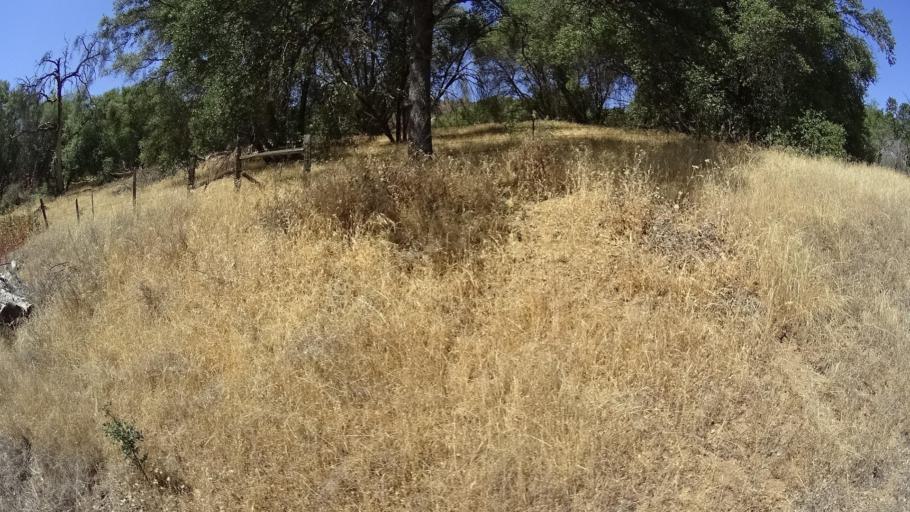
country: US
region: California
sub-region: Mariposa County
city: Mariposa
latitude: 37.3842
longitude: -119.9685
